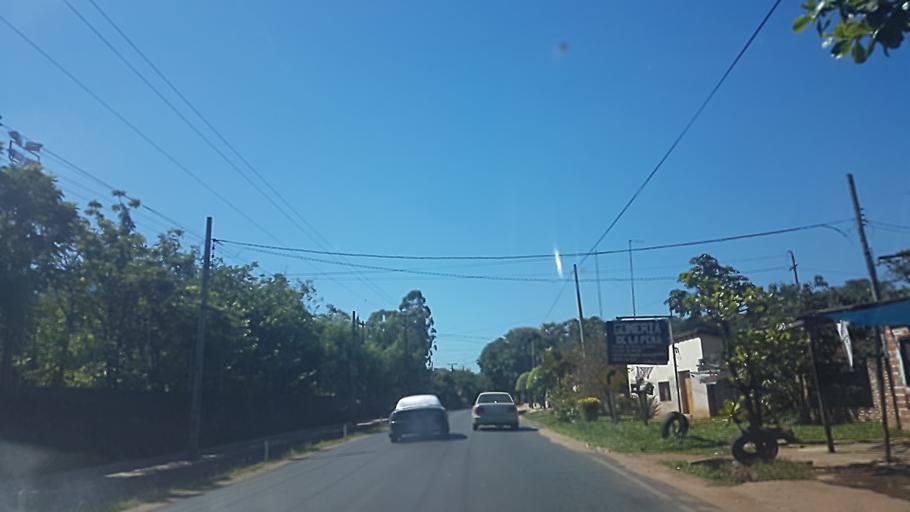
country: PY
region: Central
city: Limpio
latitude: -25.2488
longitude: -57.5034
